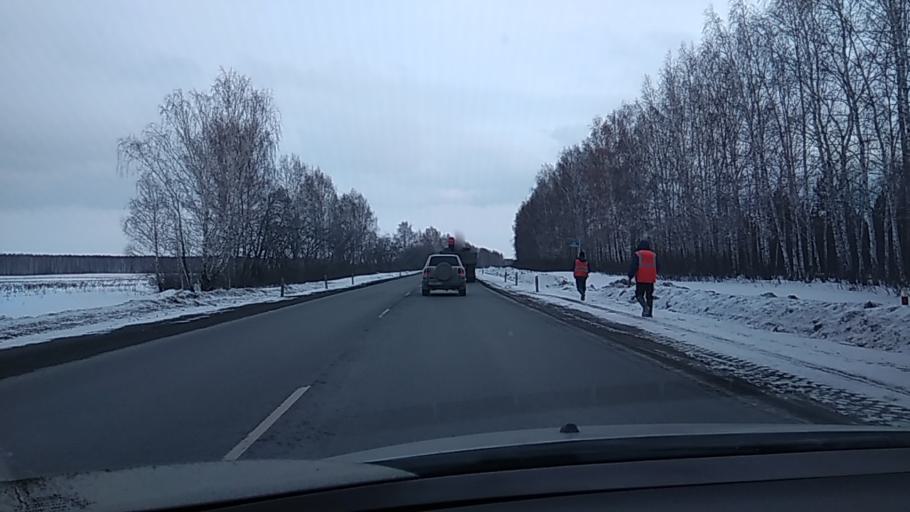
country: RU
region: Sverdlovsk
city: Sovkhoznyy
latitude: 56.5137
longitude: 61.4525
